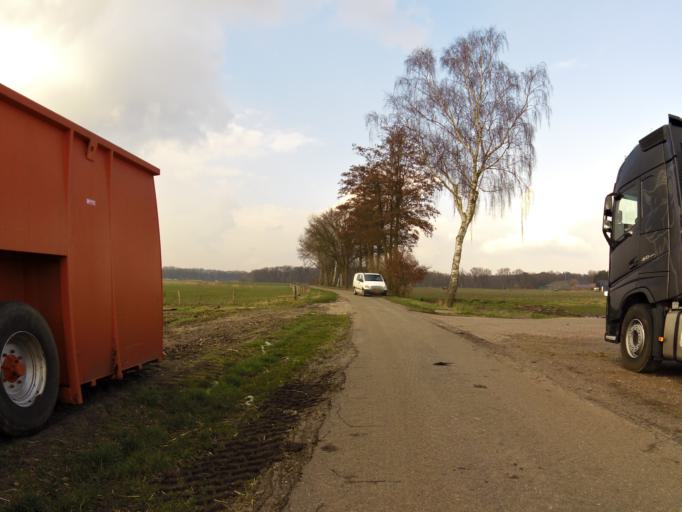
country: NL
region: North Brabant
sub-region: Gemeente Vught
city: Vught
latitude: 51.6240
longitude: 5.3096
